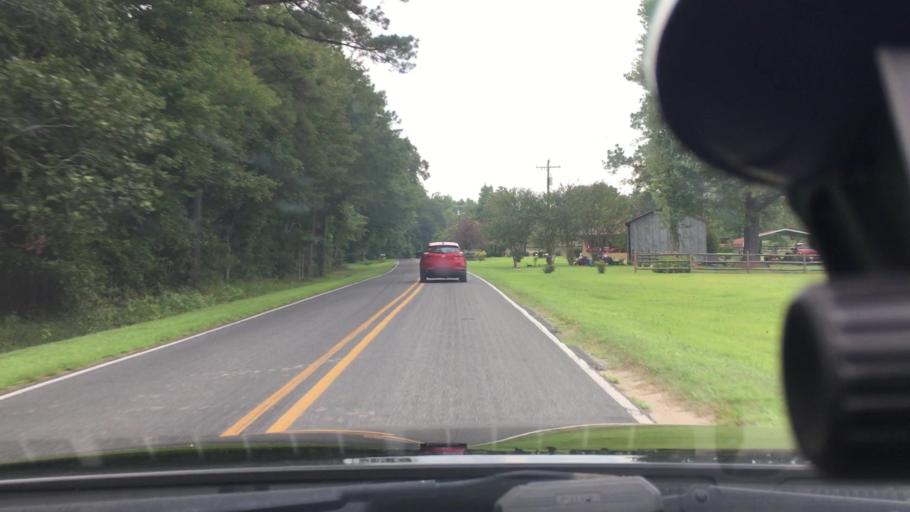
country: US
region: North Carolina
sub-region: Craven County
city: New Bern
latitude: 35.1781
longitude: -77.0545
